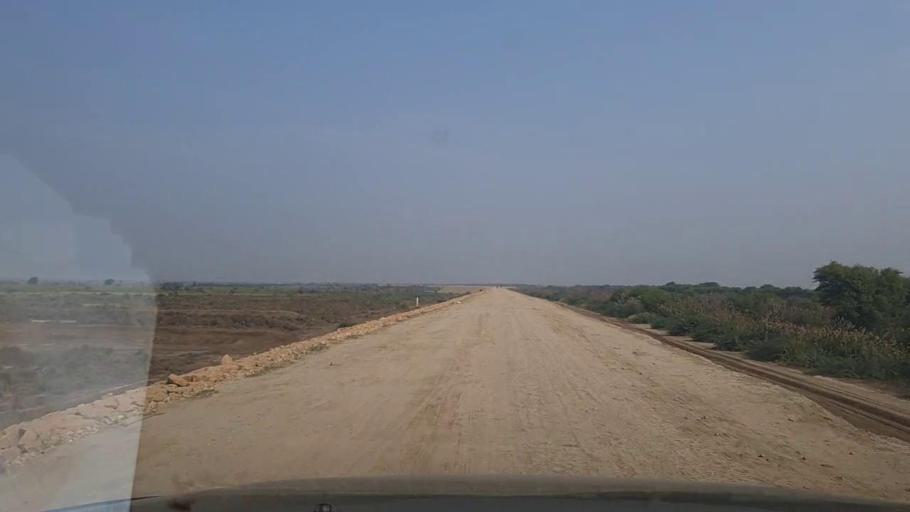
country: PK
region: Sindh
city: Bulri
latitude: 24.9511
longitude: 68.2902
